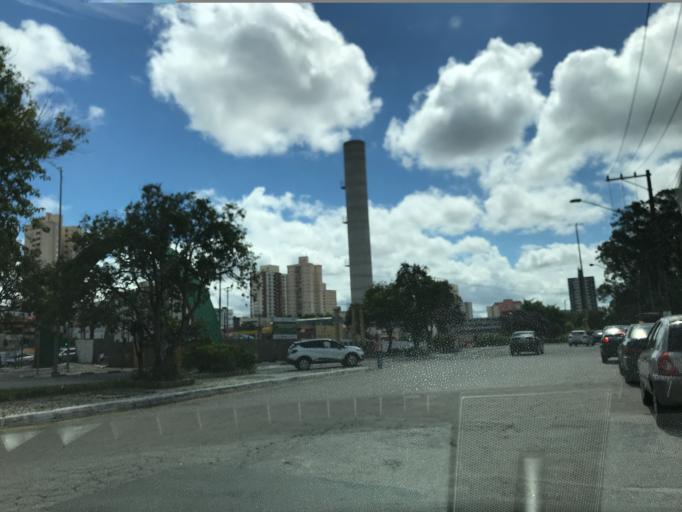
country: BR
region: Sao Paulo
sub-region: Osasco
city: Osasco
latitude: -23.5485
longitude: -46.7582
